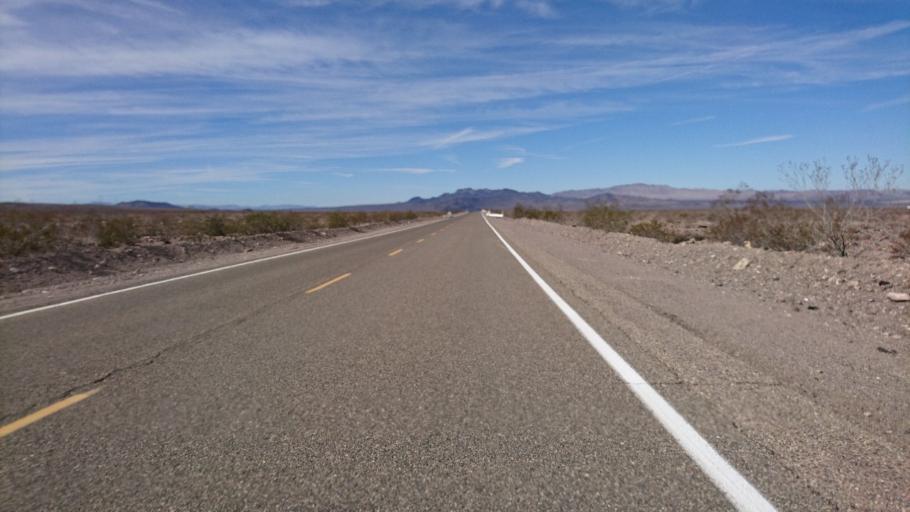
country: US
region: California
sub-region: San Bernardino County
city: Twentynine Palms
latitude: 34.7156
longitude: -116.1039
